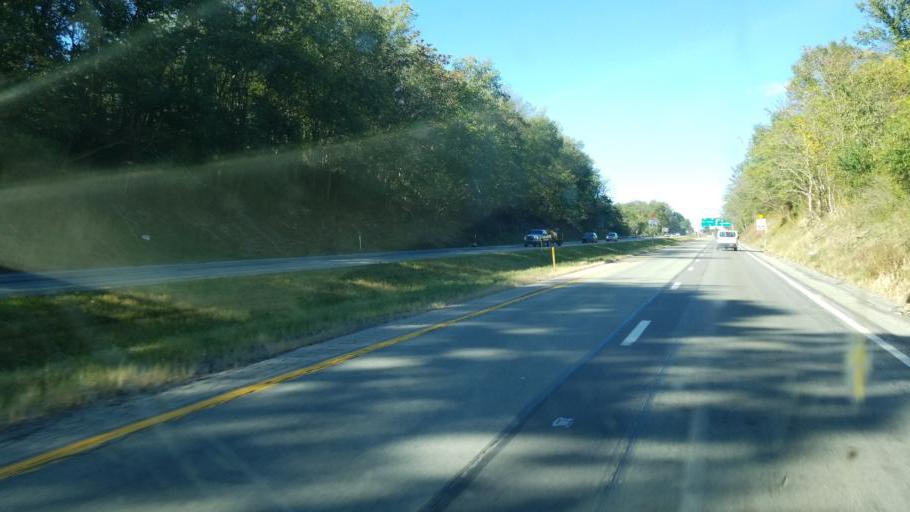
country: US
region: Pennsylvania
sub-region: Washington County
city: East Washington
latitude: 40.1379
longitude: -80.2068
